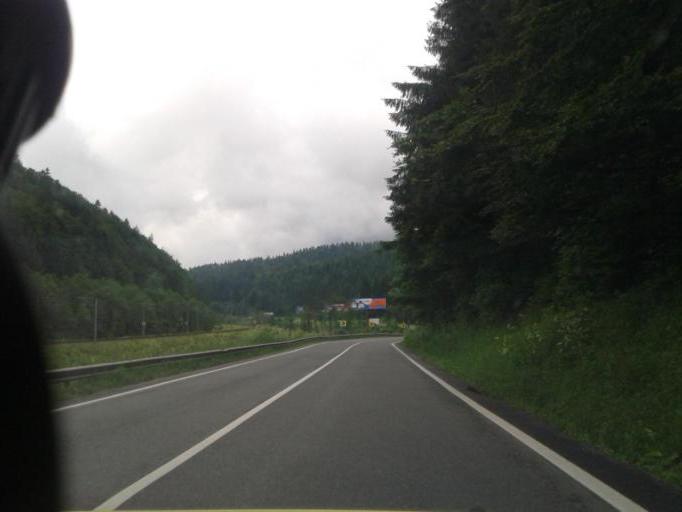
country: RO
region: Prahova
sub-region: Oras Azuga
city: Azuga
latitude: 45.4528
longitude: 25.5643
